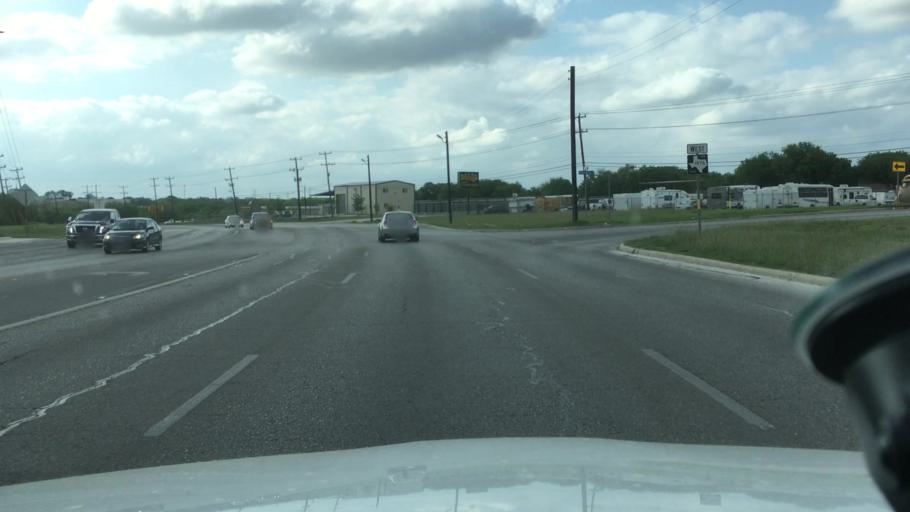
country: US
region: Texas
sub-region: Bexar County
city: Windcrest
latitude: 29.4989
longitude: -98.3505
